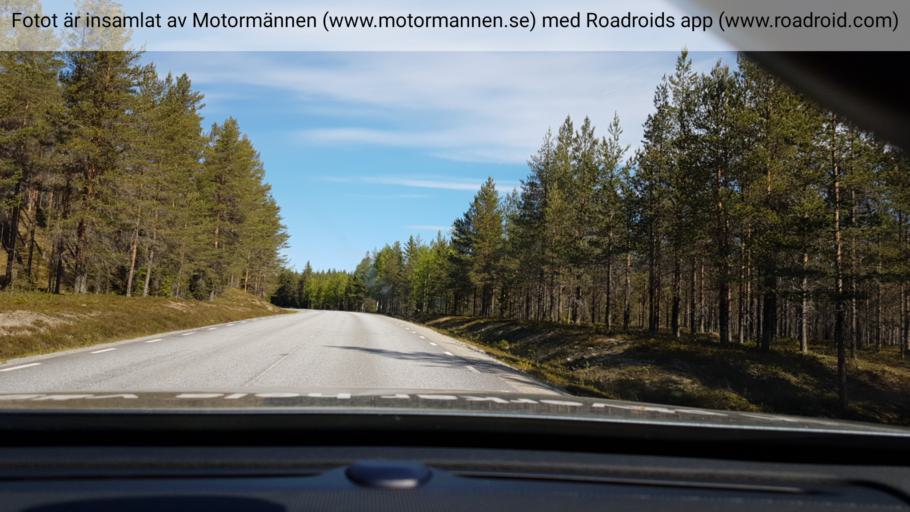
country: SE
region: Vaesterbotten
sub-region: Bjurholms Kommun
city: Bjurholm
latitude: 63.9957
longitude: 18.7925
